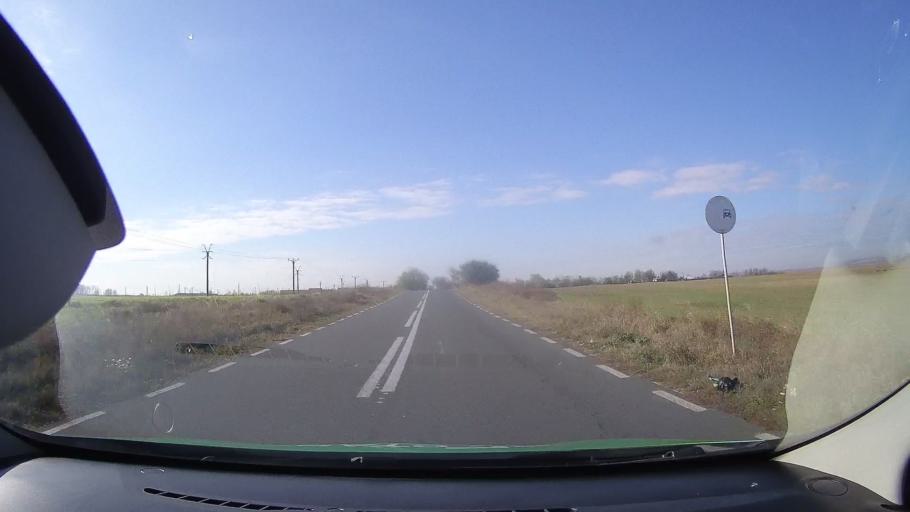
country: RO
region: Tulcea
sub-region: Comuna Murighiol
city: Murighiol
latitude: 45.0270
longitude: 29.1383
